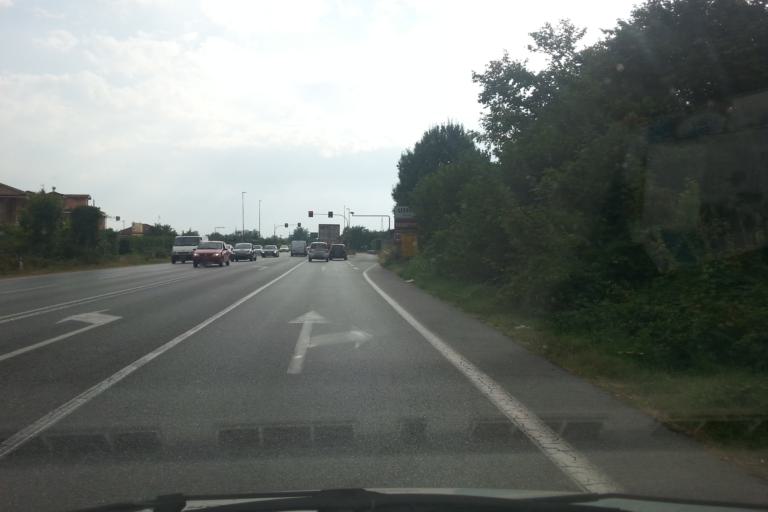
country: IT
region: Piedmont
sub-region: Provincia di Torino
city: Gerbole-Zucche
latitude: 44.9932
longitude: 7.5172
